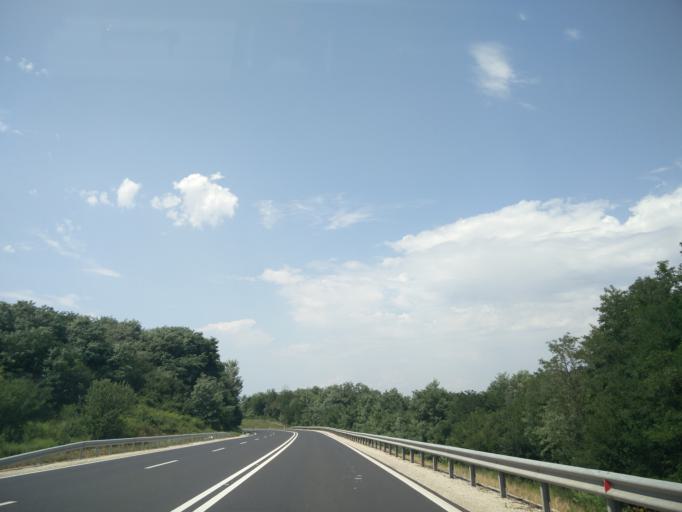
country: HU
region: Vas
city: Vasvar
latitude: 47.1001
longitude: 16.8900
